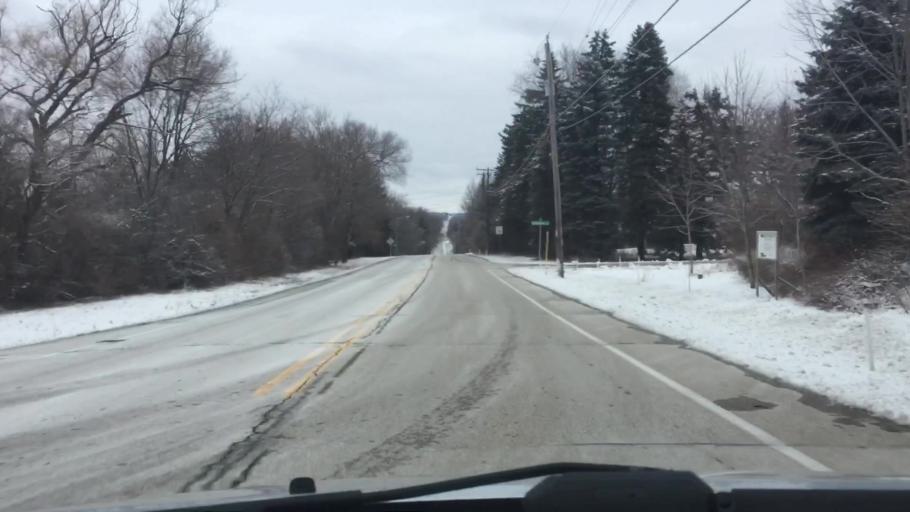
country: US
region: Wisconsin
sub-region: Waukesha County
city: Brookfield
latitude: 43.0788
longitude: -88.1059
